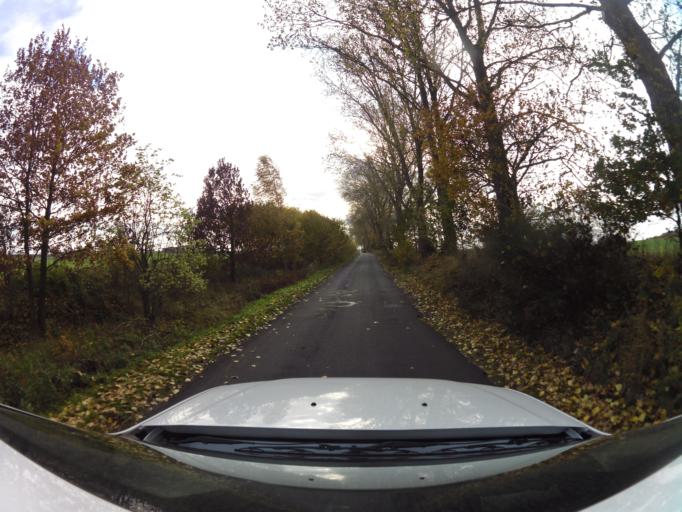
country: PL
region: West Pomeranian Voivodeship
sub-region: Powiat gryficki
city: Gryfice
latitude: 53.9012
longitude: 15.1316
